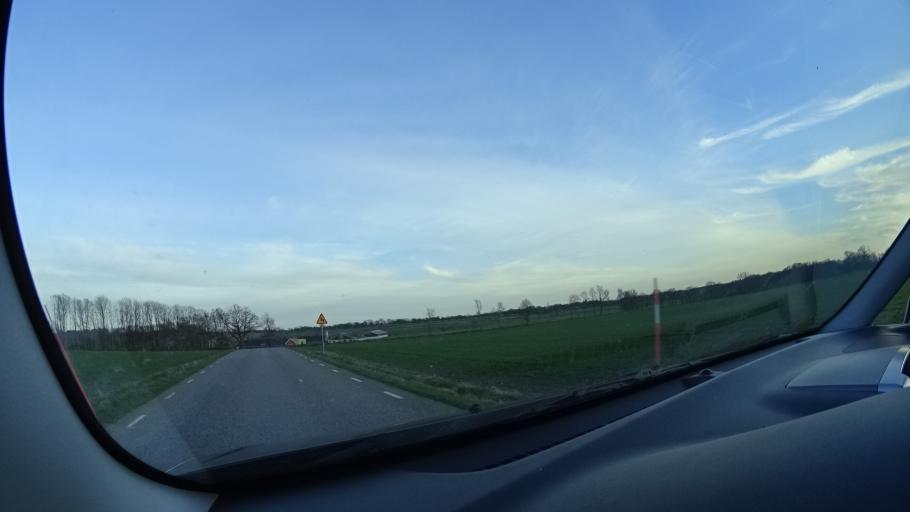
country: SE
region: Skane
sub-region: Eslovs Kommun
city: Stehag
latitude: 55.8904
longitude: 13.4239
